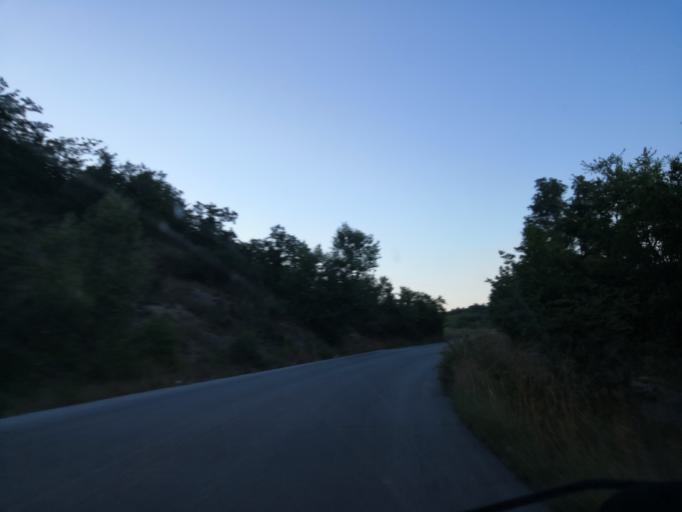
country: IT
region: Molise
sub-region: Provincia di Campobasso
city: Jelsi
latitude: 41.5103
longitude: 14.7748
